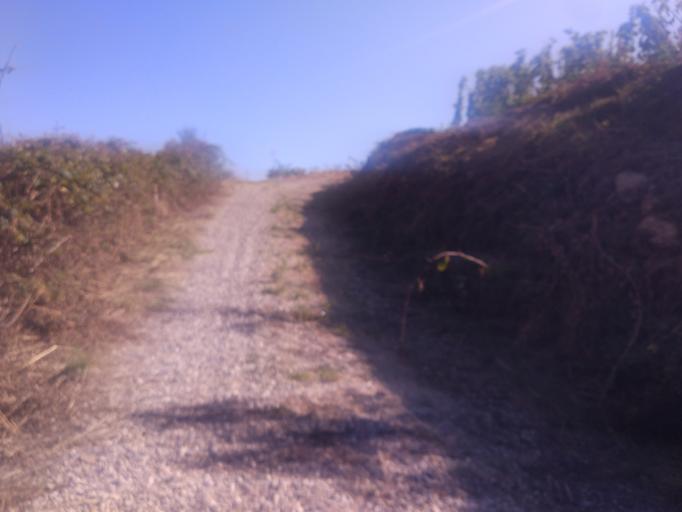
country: FR
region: Rhone-Alpes
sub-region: Departement de l'Ardeche
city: Sarras
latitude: 45.1950
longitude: 4.7657
